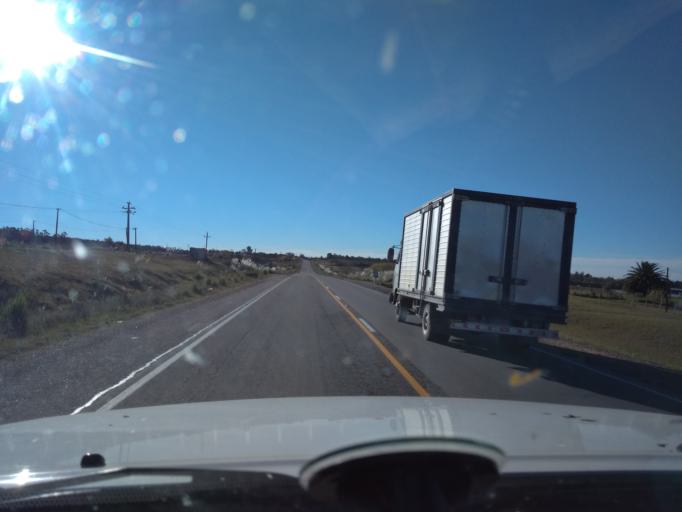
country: UY
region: Canelones
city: Sauce
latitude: -34.5884
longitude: -56.0539
